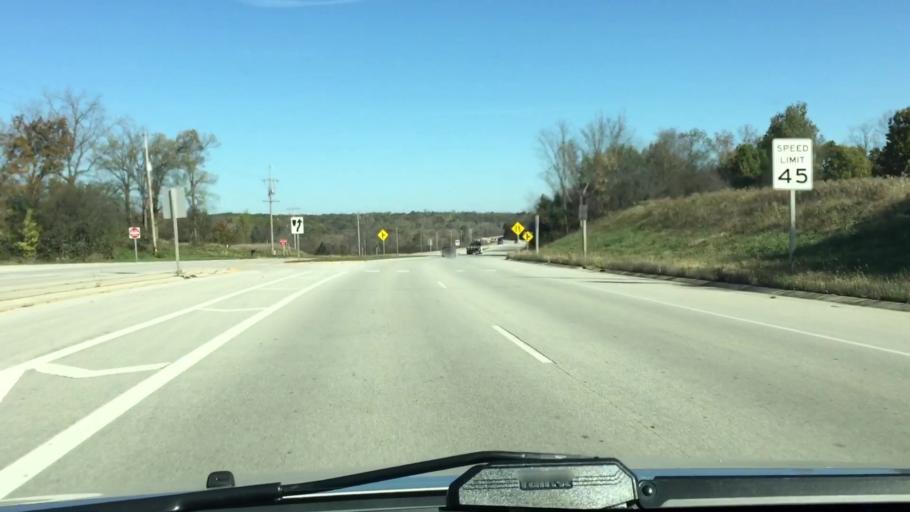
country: US
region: Wisconsin
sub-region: Waukesha County
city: Wales
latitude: 43.0164
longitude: -88.3836
